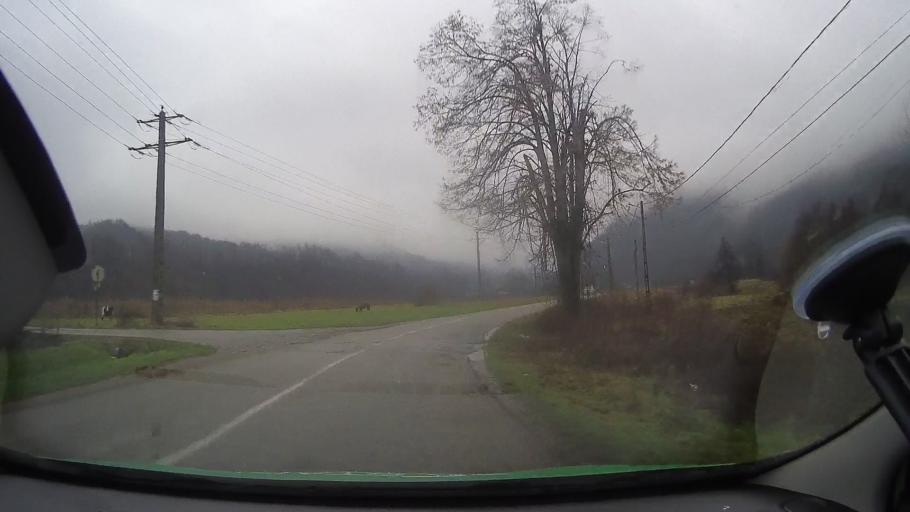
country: RO
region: Arad
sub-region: Comuna Dezna
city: Dezna
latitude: 46.4237
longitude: 22.2544
